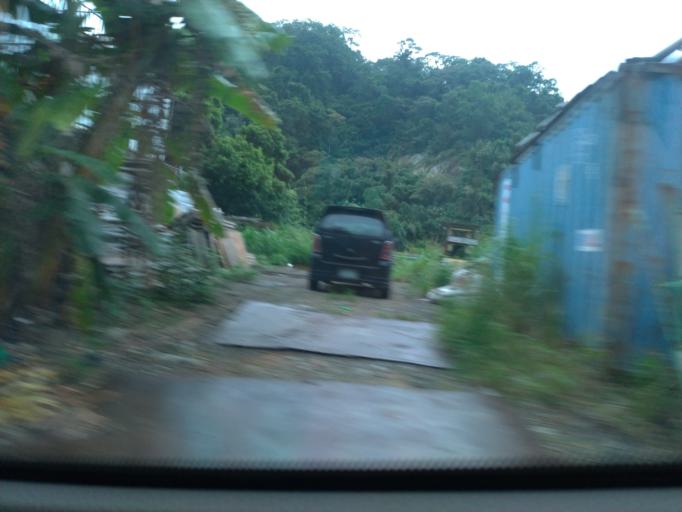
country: TW
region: Taipei
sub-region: Taipei
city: Banqiao
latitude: 24.9249
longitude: 121.4265
